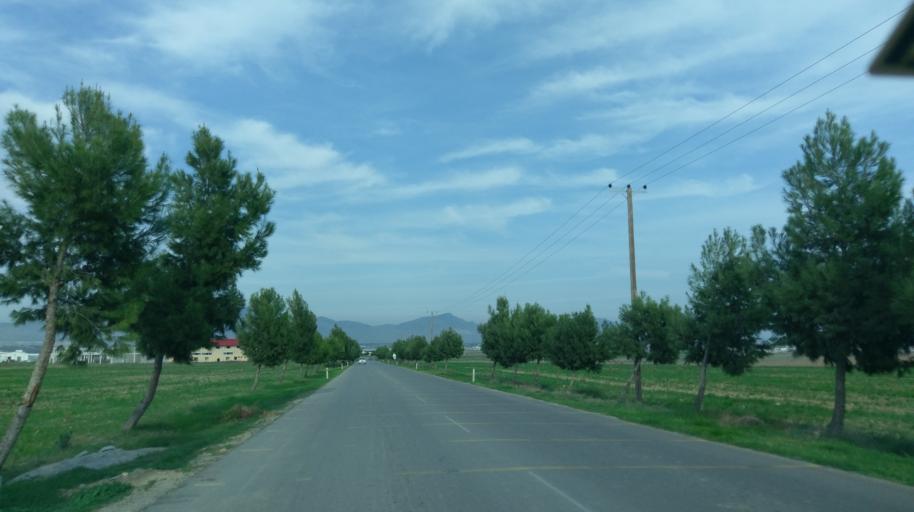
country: CY
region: Lefkosia
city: Mammari
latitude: 35.2028
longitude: 33.2716
